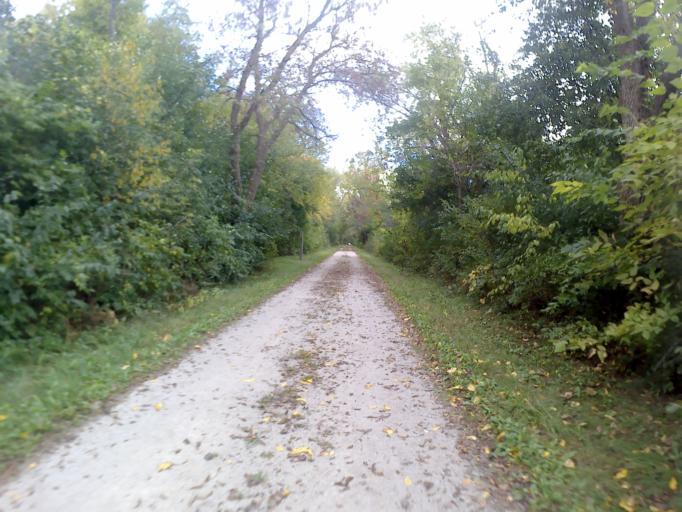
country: US
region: Illinois
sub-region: DuPage County
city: Wayne
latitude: 41.9386
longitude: -88.2279
